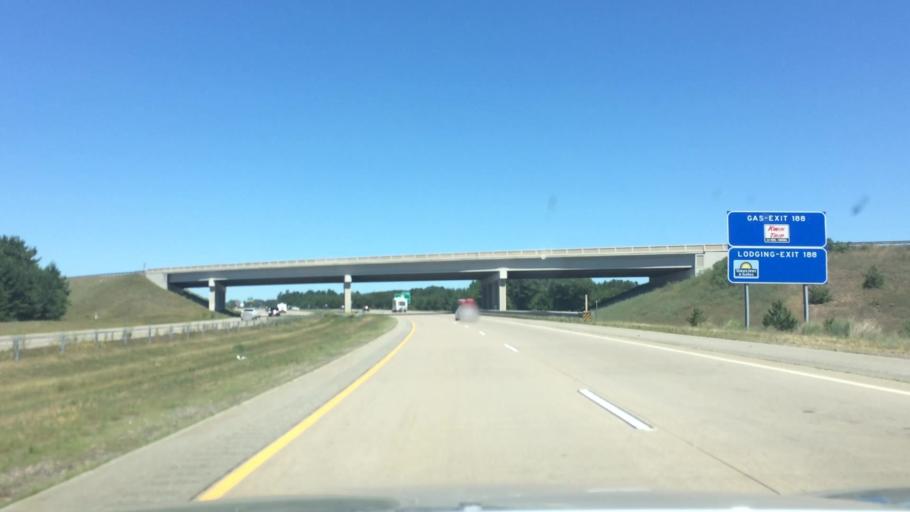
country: US
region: Wisconsin
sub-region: Marathon County
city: Rothschild
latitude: 44.8955
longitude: -89.6400
